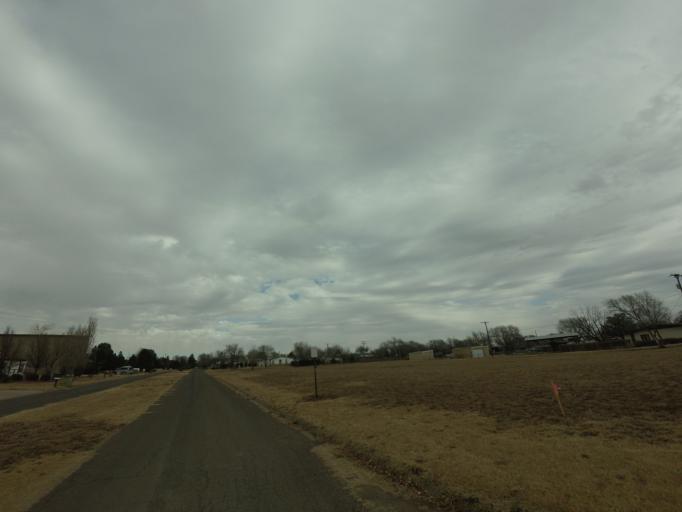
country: US
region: New Mexico
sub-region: Curry County
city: Clovis
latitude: 34.3757
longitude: -103.2010
